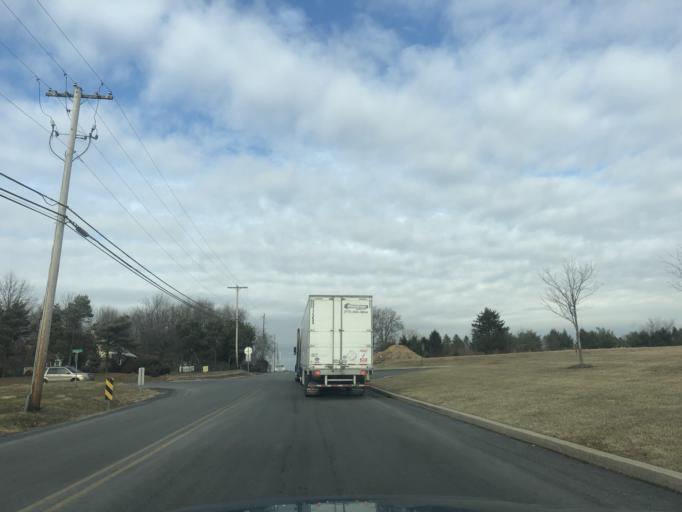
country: US
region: Pennsylvania
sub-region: Bucks County
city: Spinnerstown
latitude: 40.4367
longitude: -75.4147
